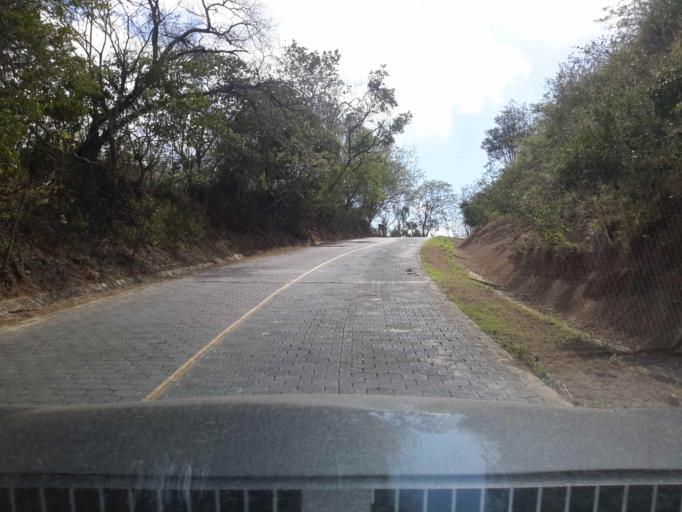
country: NI
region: Rivas
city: San Juan del Sur
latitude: 11.2231
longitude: -85.8168
